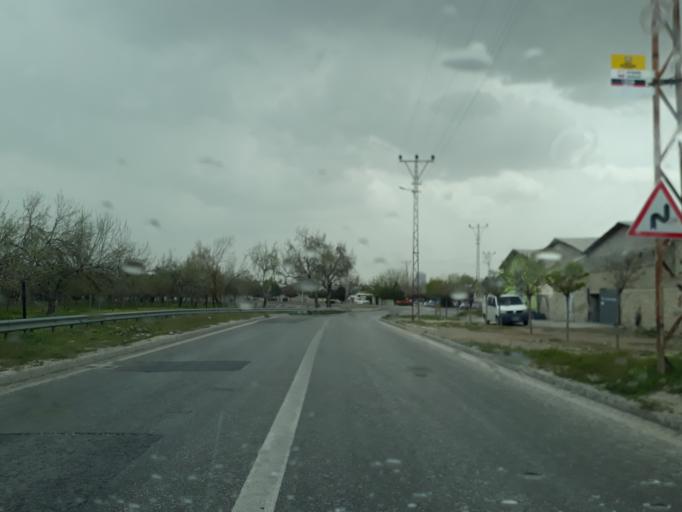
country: TR
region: Konya
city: Selcuklu
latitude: 37.9174
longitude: 32.4747
